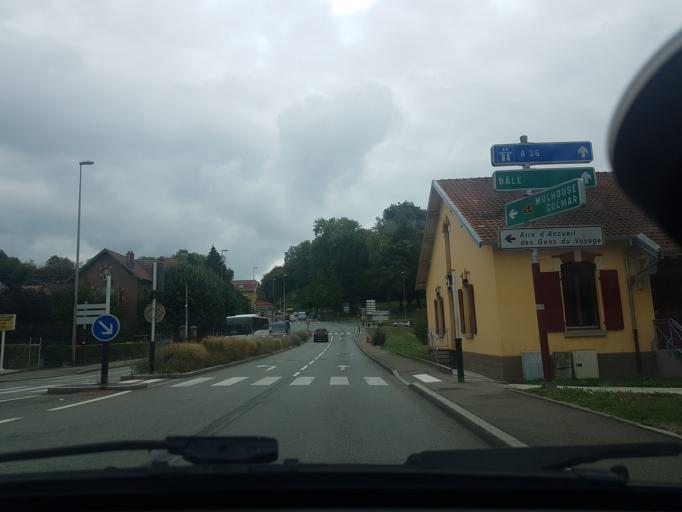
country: FR
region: Franche-Comte
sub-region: Territoire de Belfort
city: Belfort
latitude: 47.6409
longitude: 6.8667
